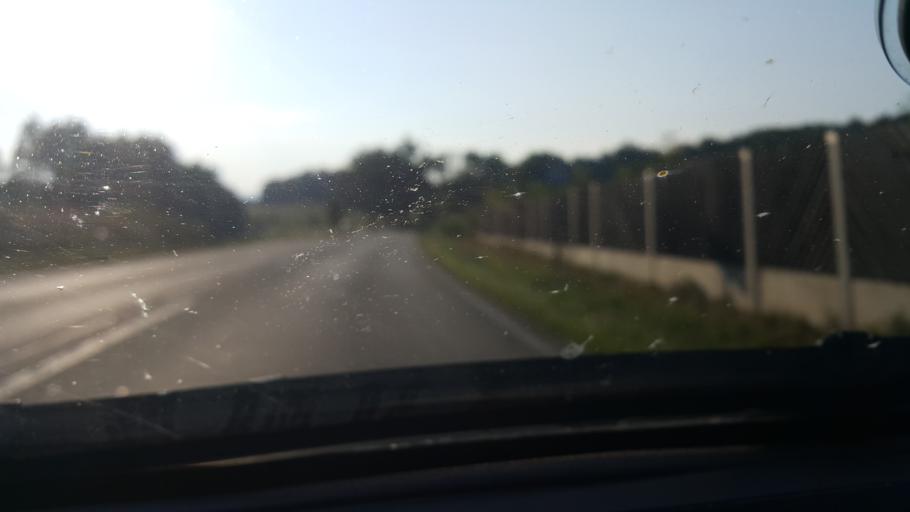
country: AT
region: Carinthia
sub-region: Klagenfurt am Woerthersee
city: Klagenfurt am Woerthersee
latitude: 46.6659
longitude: 14.2700
